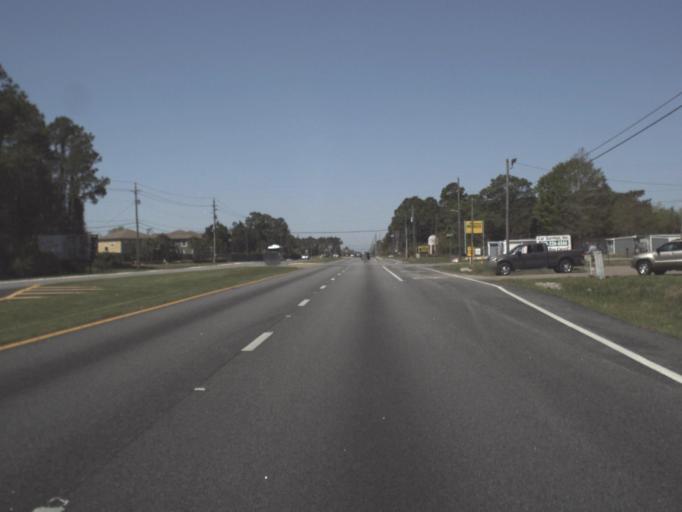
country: US
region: Florida
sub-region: Okaloosa County
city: Mary Esther
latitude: 30.4120
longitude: -86.7383
